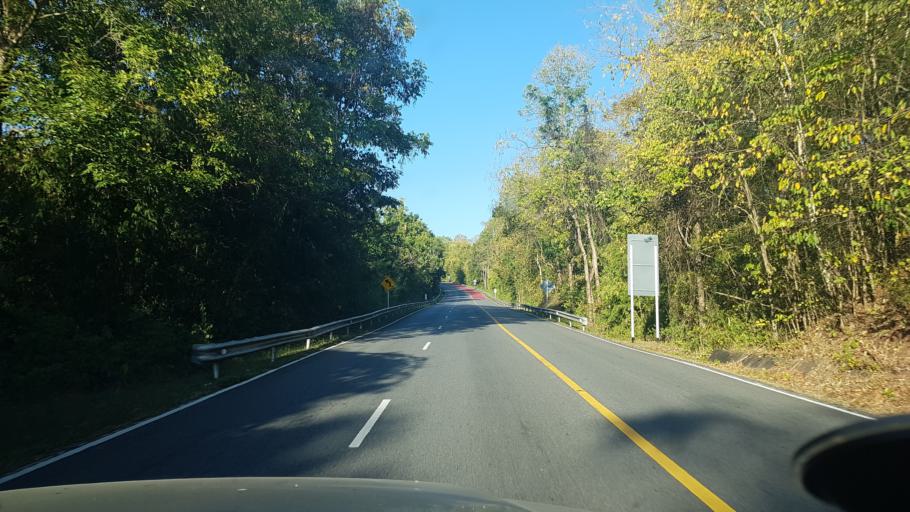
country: TH
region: Phetchabun
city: Nam Nao
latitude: 16.7028
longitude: 101.6599
